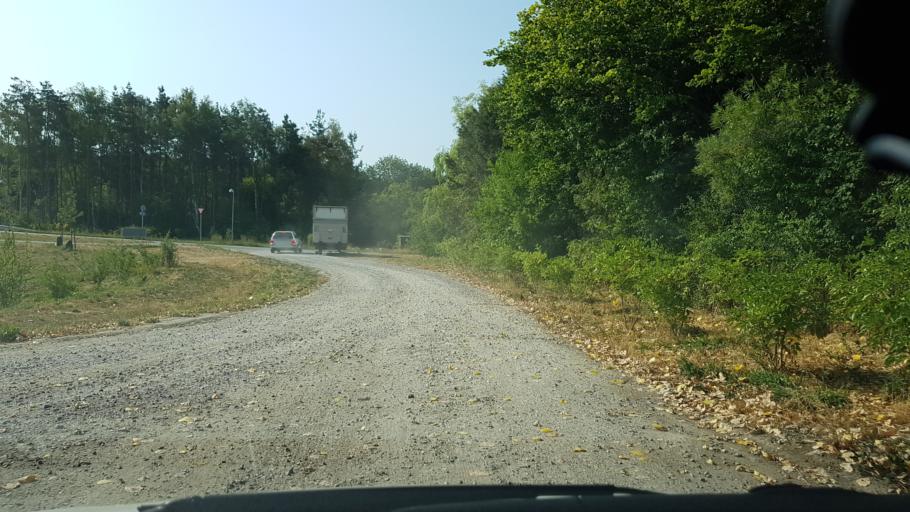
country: DK
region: Capital Region
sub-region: Vallensbaek Kommune
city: Vallensbaek
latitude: 55.6416
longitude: 12.3822
